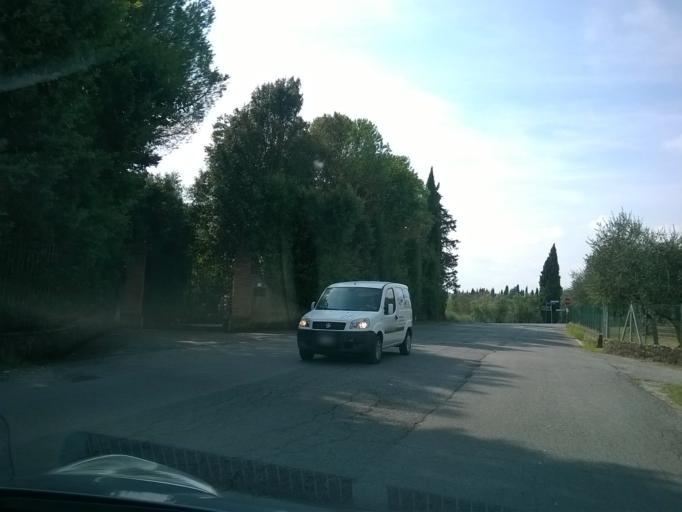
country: IT
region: Tuscany
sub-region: Provincia di Pistoia
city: Pescia
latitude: 43.8931
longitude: 10.6822
